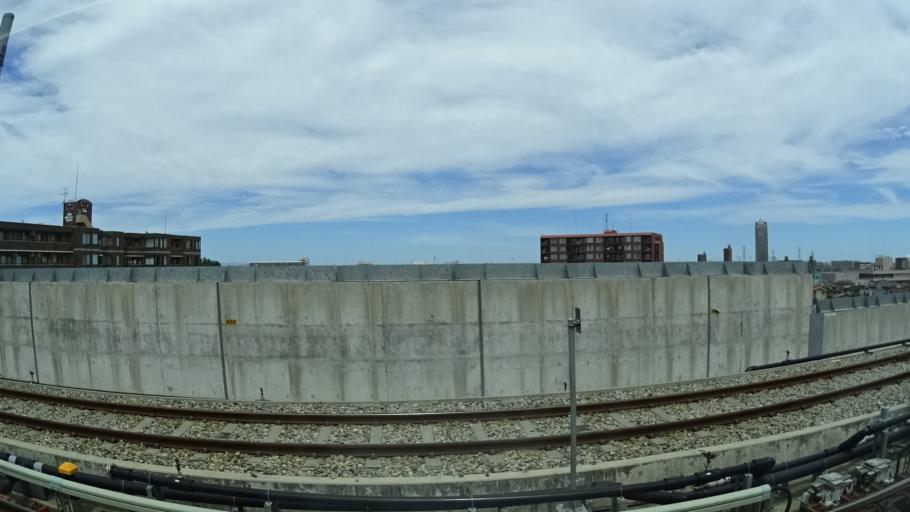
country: JP
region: Toyama
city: Toyama-shi
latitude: 36.6986
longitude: 137.2239
